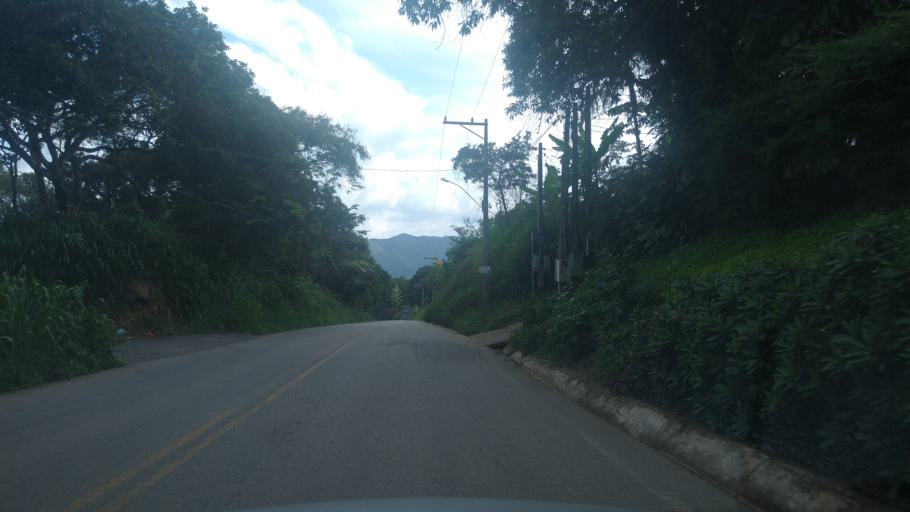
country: BR
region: Minas Gerais
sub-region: Extrema
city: Extrema
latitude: -22.8055
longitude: -46.3143
